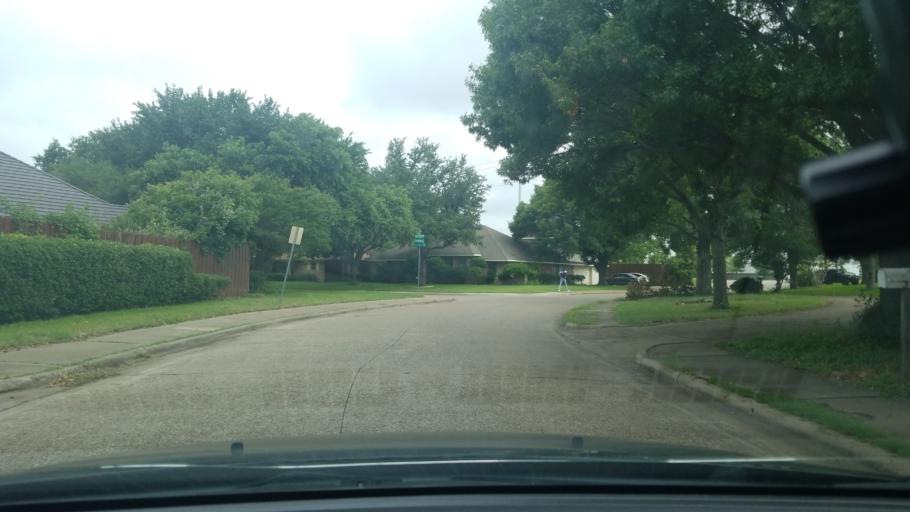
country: US
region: Texas
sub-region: Dallas County
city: Balch Springs
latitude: 32.7914
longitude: -96.6881
